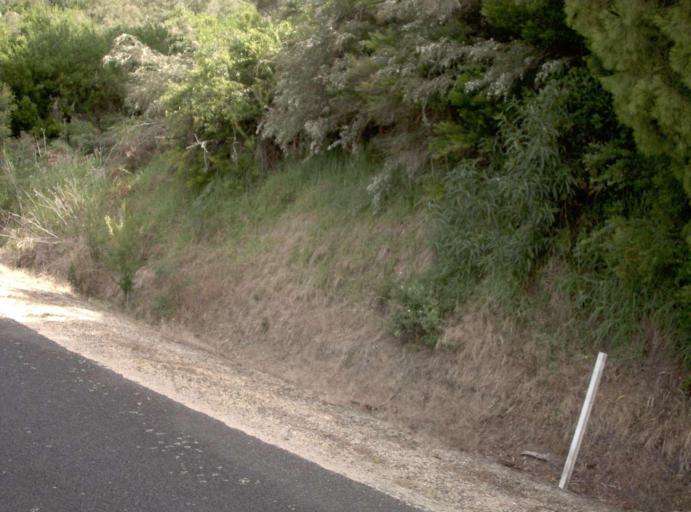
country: AU
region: New South Wales
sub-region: Bega Valley
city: Eden
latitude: -37.4779
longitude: 149.5962
